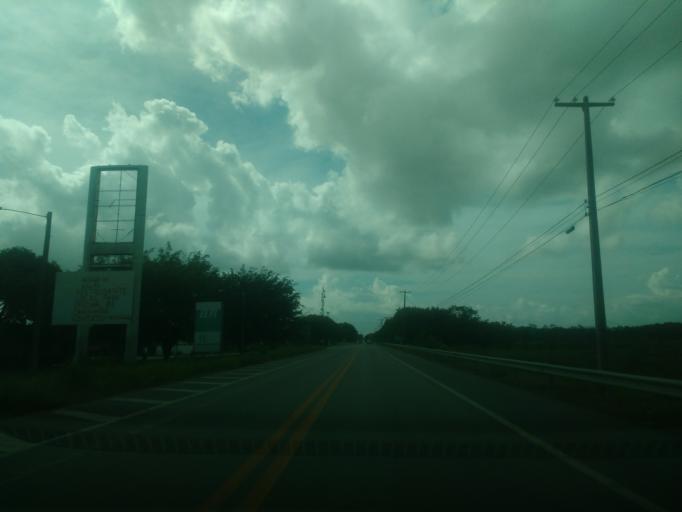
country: BR
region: Alagoas
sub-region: Marechal Deodoro
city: Marechal Deodoro
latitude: -9.6709
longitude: -35.8408
